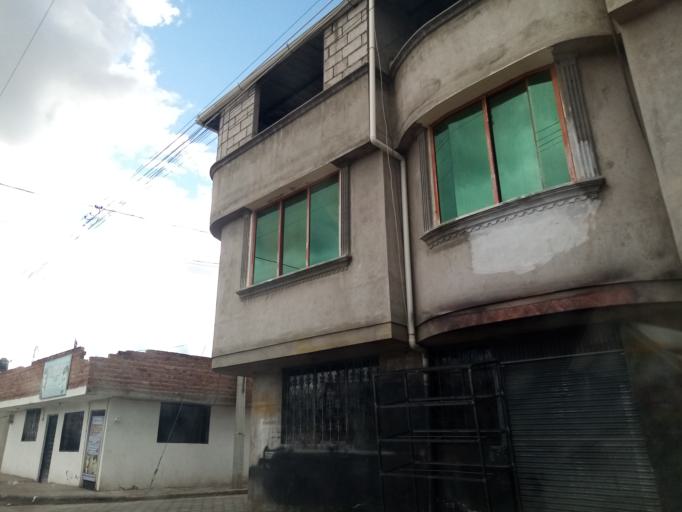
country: EC
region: Chimborazo
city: Riobamba
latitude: -1.6894
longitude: -78.6269
